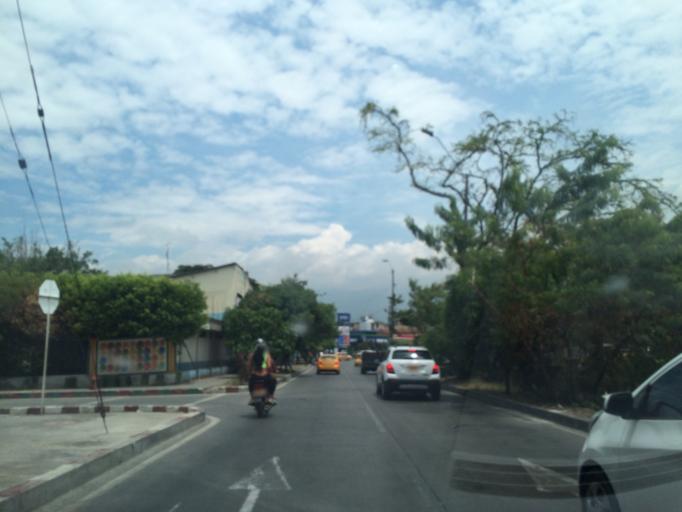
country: CO
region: Valle del Cauca
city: Cali
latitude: 3.4182
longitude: -76.5264
